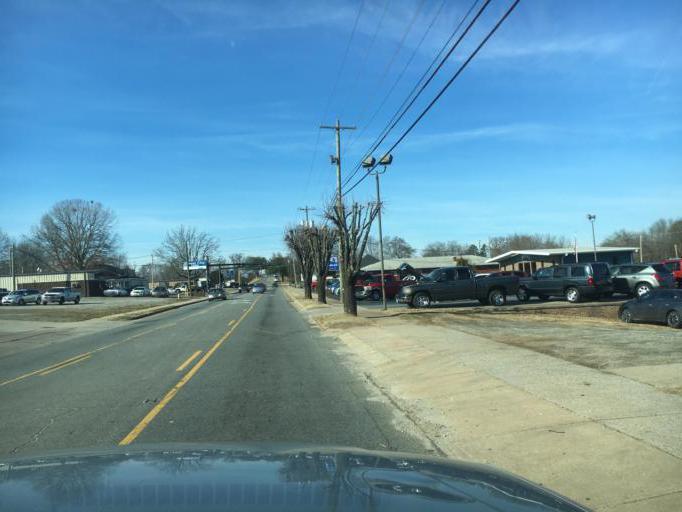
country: US
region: North Carolina
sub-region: Rutherford County
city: Forest City
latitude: 35.3260
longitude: -81.8614
